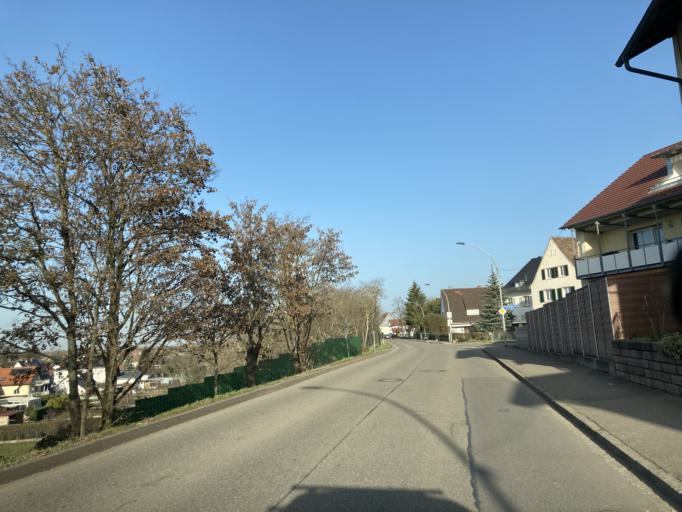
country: DE
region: Baden-Wuerttemberg
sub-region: Freiburg Region
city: Neuenburg am Rhein
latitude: 47.8172
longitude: 7.5624
